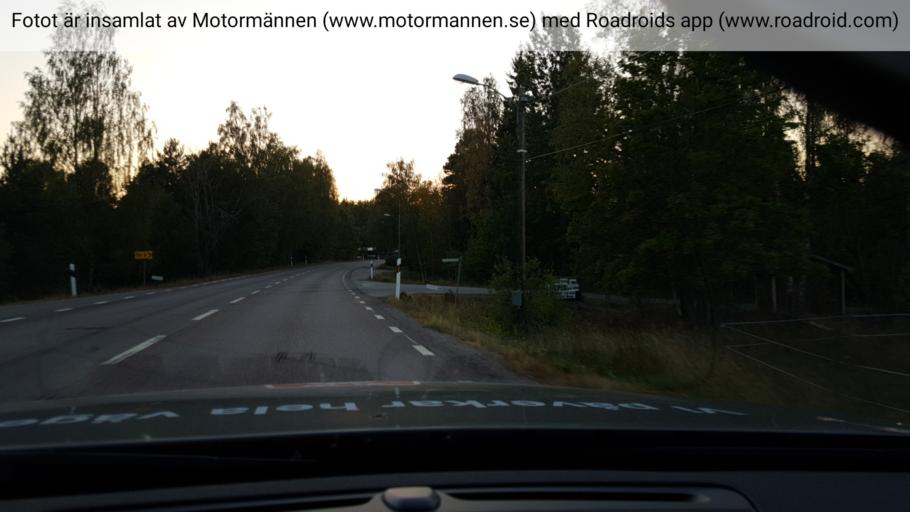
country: SE
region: Uppsala
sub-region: Heby Kommun
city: OEstervala
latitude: 60.0727
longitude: 17.2088
